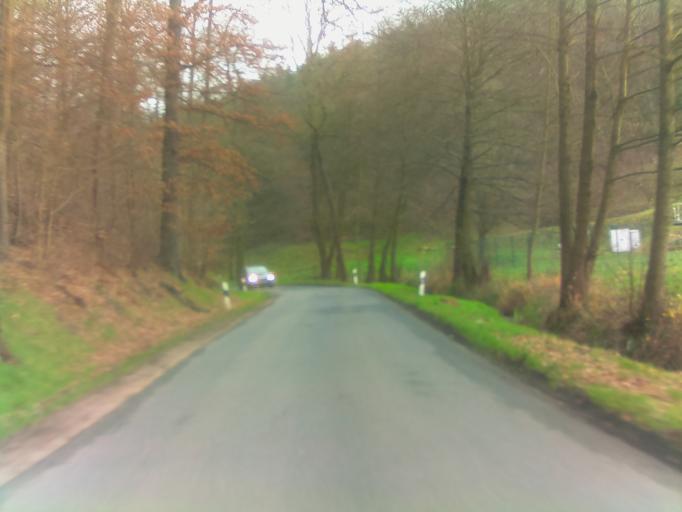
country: DE
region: Thuringia
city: Grosspurschutz
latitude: 50.8239
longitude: 11.6105
